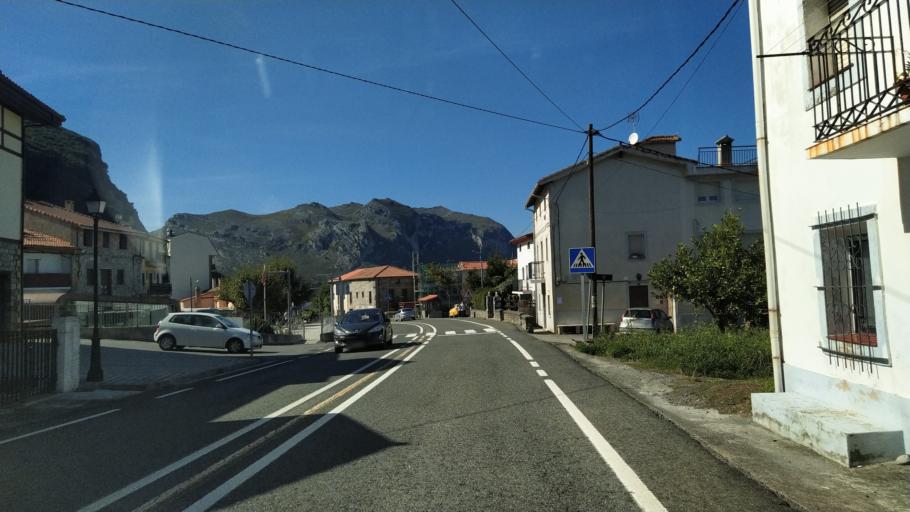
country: ES
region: Cantabria
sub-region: Provincia de Cantabria
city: Liendo
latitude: 43.4041
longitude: -3.2988
